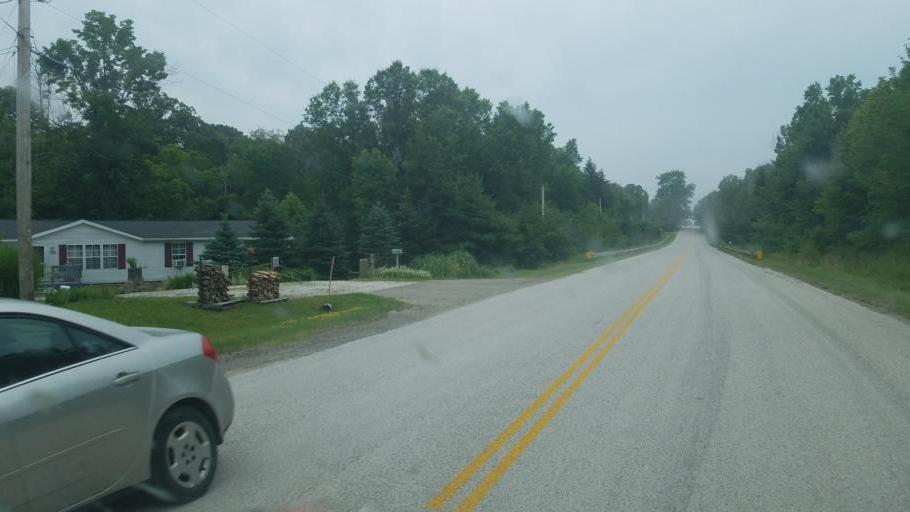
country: US
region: Ohio
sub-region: Mahoning County
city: Craig Beach
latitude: 41.1426
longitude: -81.0513
